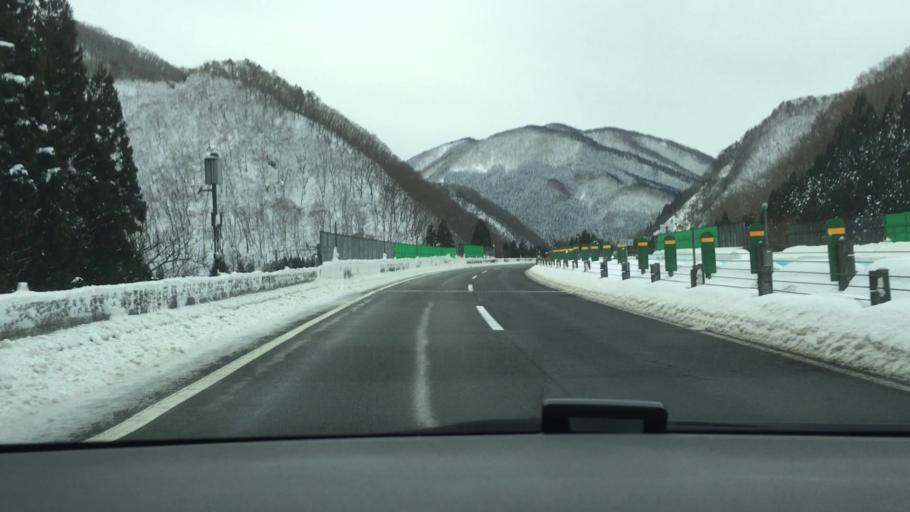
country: JP
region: Akita
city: Hanawa
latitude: 40.1221
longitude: 140.9059
